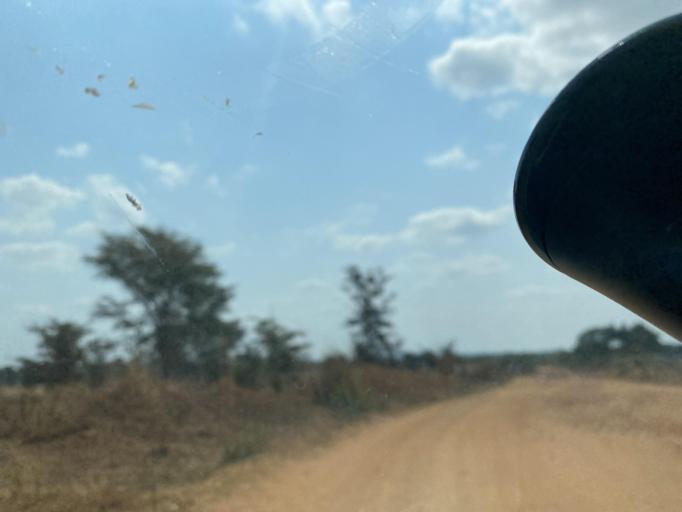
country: ZM
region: Lusaka
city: Chongwe
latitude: -15.5880
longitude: 28.7692
